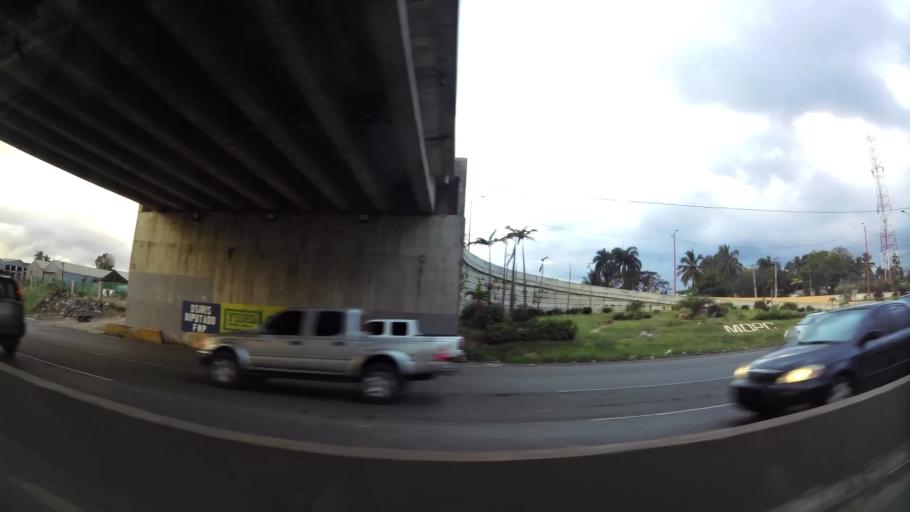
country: DO
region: Santo Domingo
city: Santo Domingo Oeste
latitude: 18.5471
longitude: -70.0410
